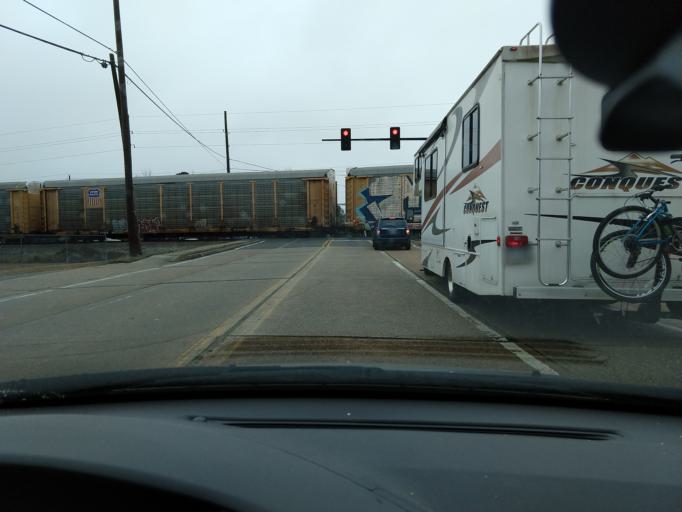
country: US
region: Mississippi
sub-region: Jackson County
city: Ocean Springs
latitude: 30.4125
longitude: -88.7955
